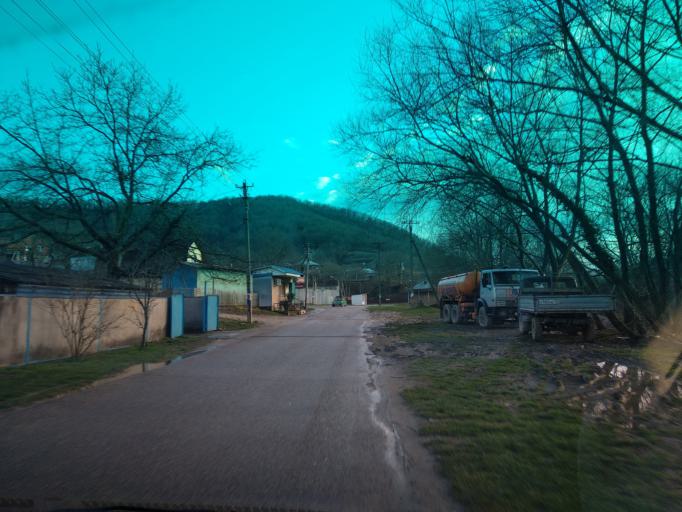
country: RU
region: Krasnodarskiy
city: Novomikhaylovskiy
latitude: 44.2722
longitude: 38.8325
